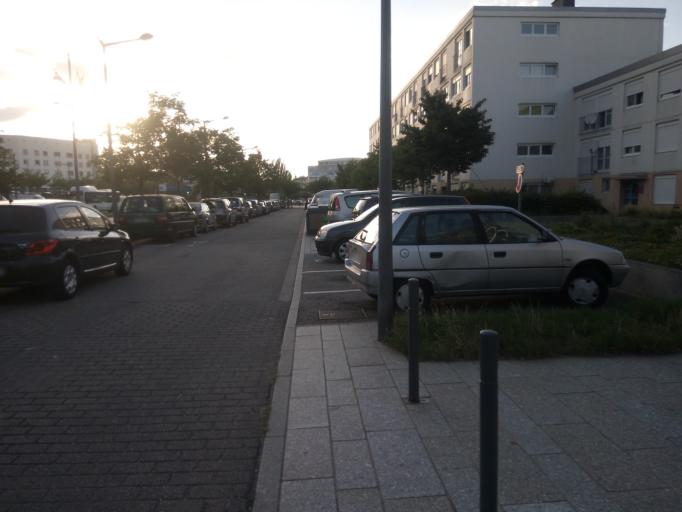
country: FR
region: Lorraine
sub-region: Departement de Meurthe-et-Moselle
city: Villers-les-Nancy
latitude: 48.6648
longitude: 6.1690
